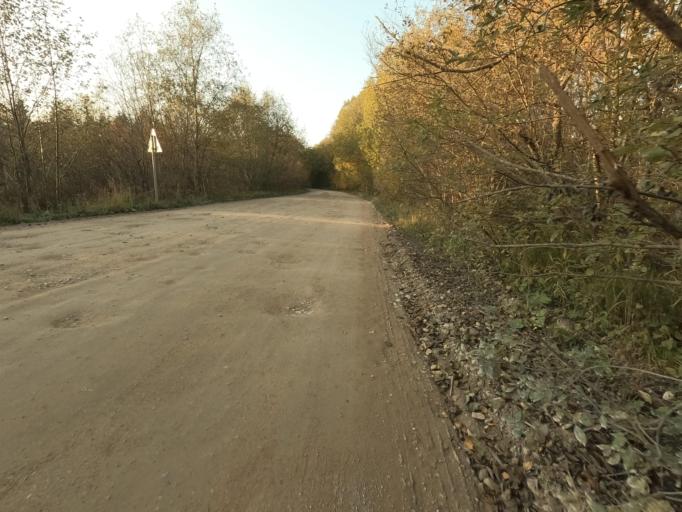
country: RU
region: Leningrad
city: Lyuban'
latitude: 59.0023
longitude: 31.0984
